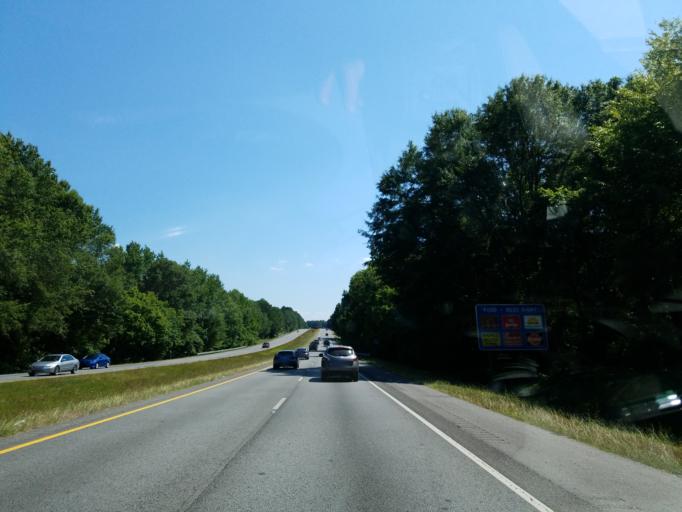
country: US
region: Georgia
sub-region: Spalding County
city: Experiment
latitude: 33.2594
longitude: -84.2920
